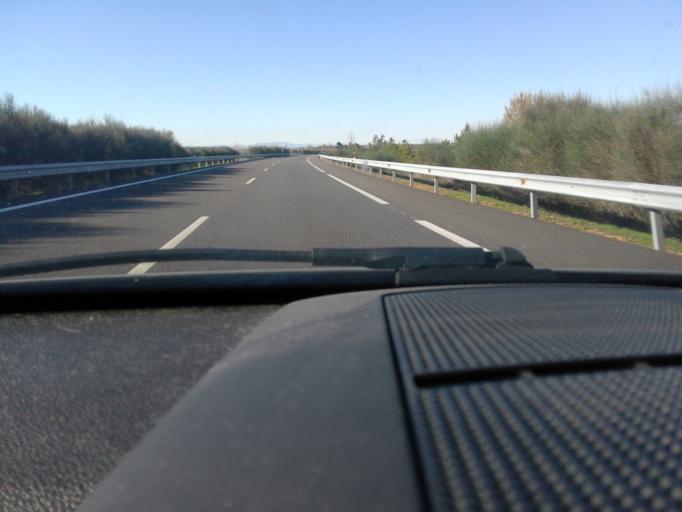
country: ES
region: Castille and Leon
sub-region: Provincia de Leon
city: Villanueva de las Manzanas
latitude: 42.4586
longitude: -5.4411
